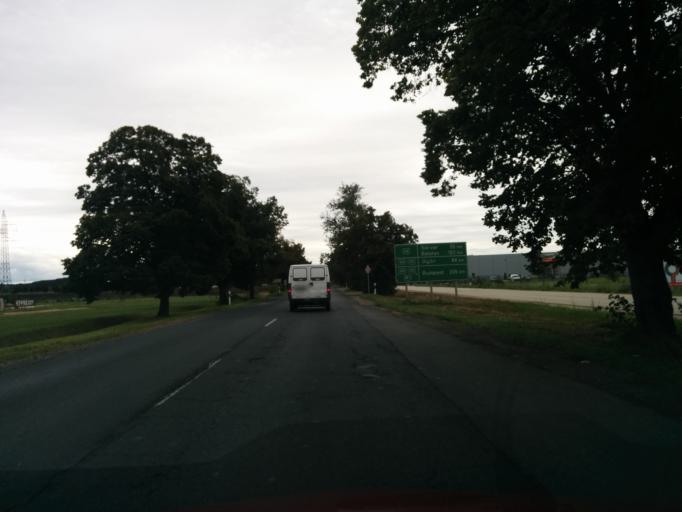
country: HU
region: Gyor-Moson-Sopron
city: Sopron
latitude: 47.6678
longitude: 16.6189
